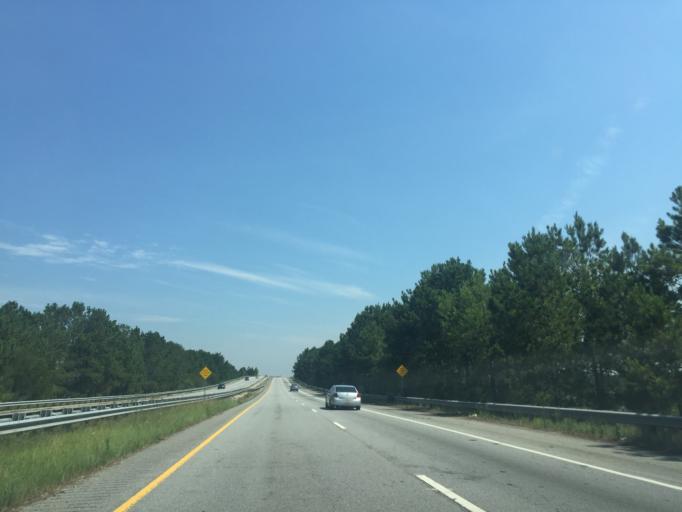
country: US
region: Georgia
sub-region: Chatham County
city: Georgetown
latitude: 31.9947
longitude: -81.2000
